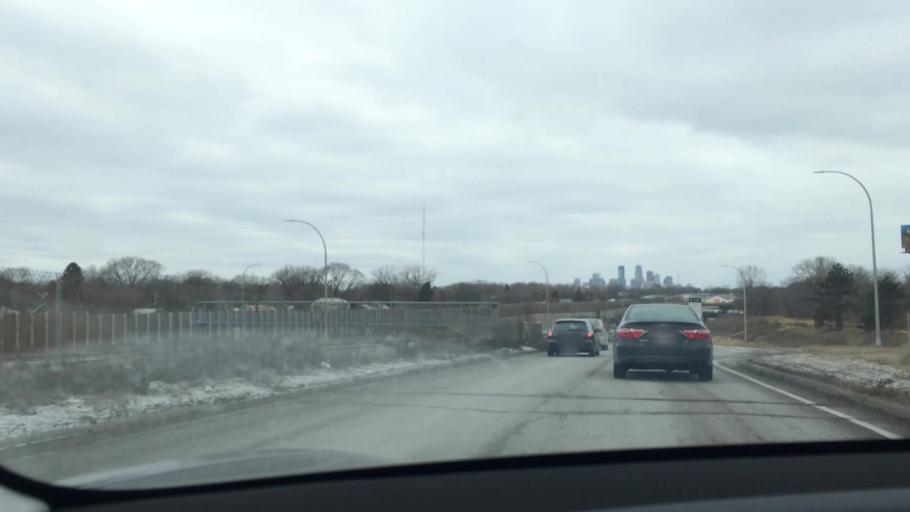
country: US
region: Minnesota
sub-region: Ramsey County
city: Lauderdale
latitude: 44.9569
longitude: -93.1930
